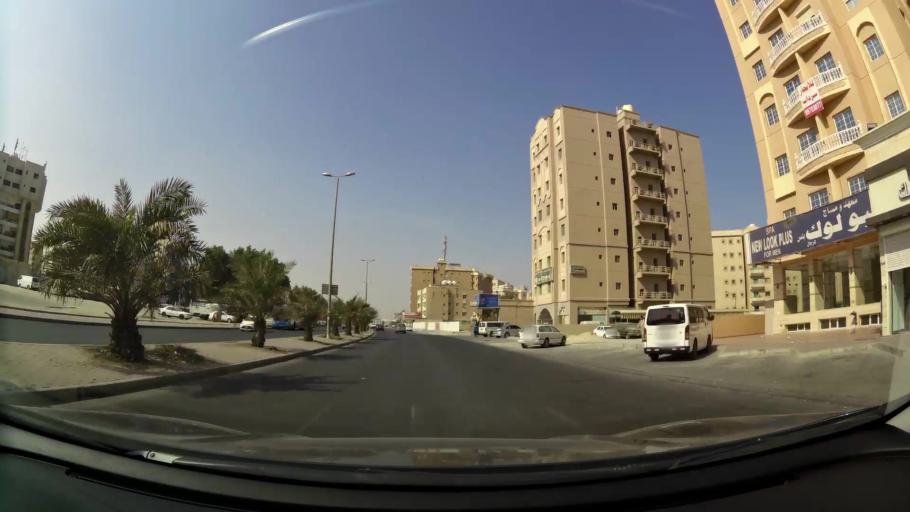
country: KW
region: Al Ahmadi
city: Al Manqaf
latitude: 29.0961
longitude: 48.1292
